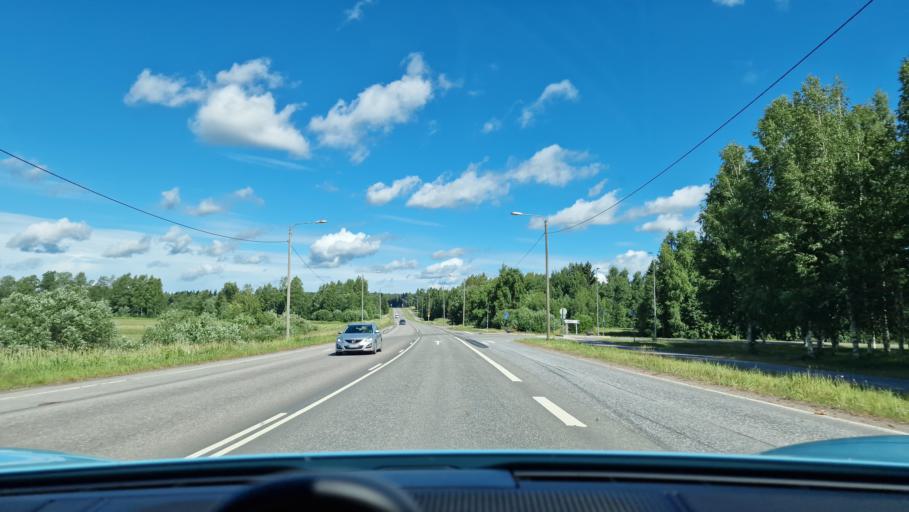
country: FI
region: Pirkanmaa
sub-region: Tampere
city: Orivesi
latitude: 61.6681
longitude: 24.3557
